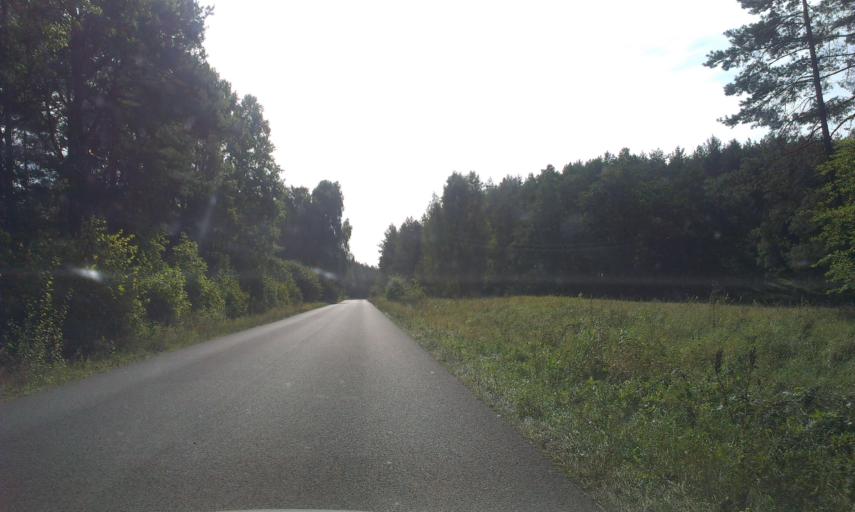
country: PL
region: Greater Poland Voivodeship
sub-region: Powiat zlotowski
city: Zlotow
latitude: 53.4850
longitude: 16.9920
